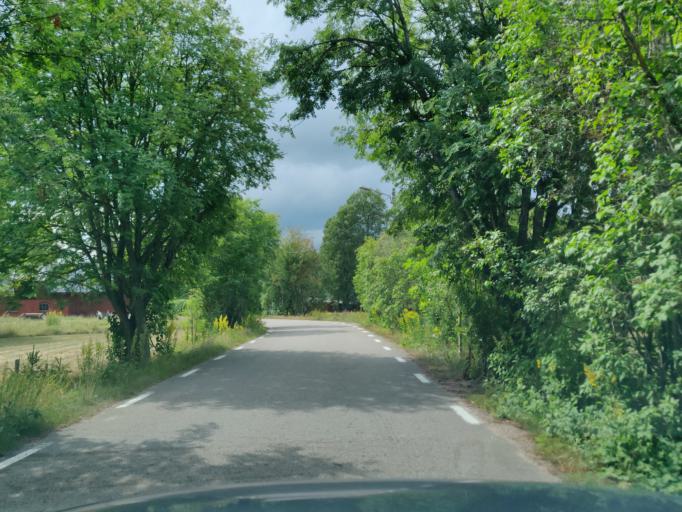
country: SE
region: Vaermland
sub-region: Munkfors Kommun
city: Munkfors
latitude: 59.8837
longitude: 13.5611
